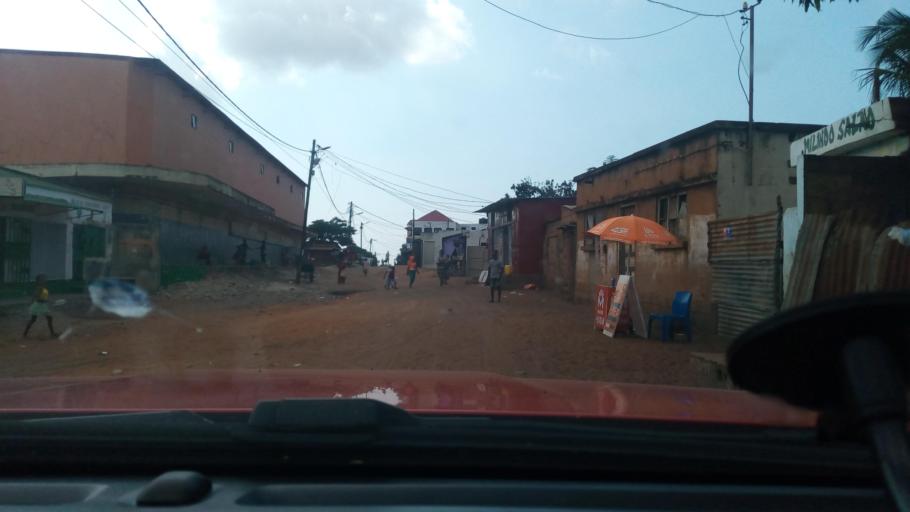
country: MZ
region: Maputo City
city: Maputo
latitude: -25.9218
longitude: 32.5935
